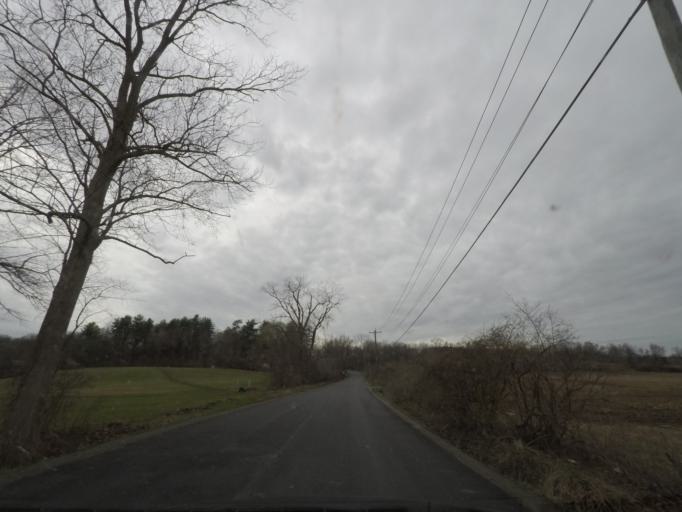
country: US
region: New York
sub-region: Rensselaer County
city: Castleton-on-Hudson
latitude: 42.5543
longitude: -73.7747
